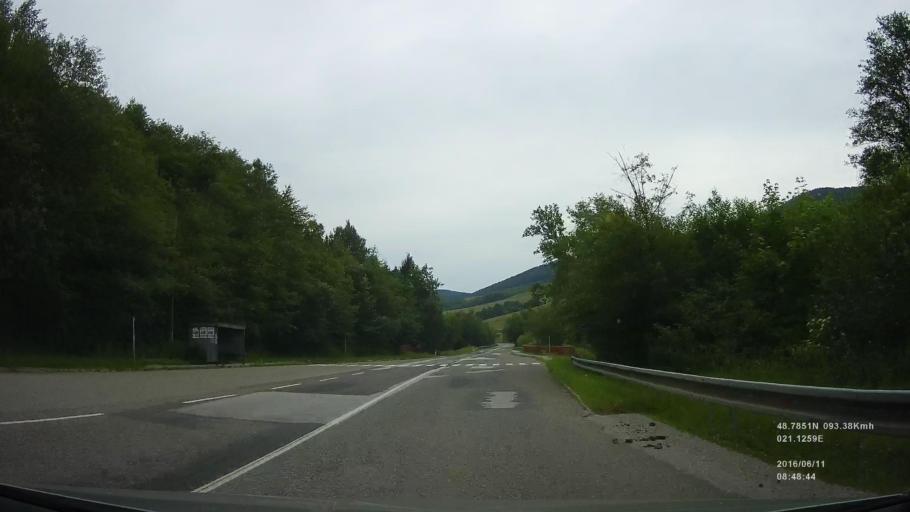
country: SK
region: Kosicky
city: Kosice
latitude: 48.7811
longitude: 21.1339
